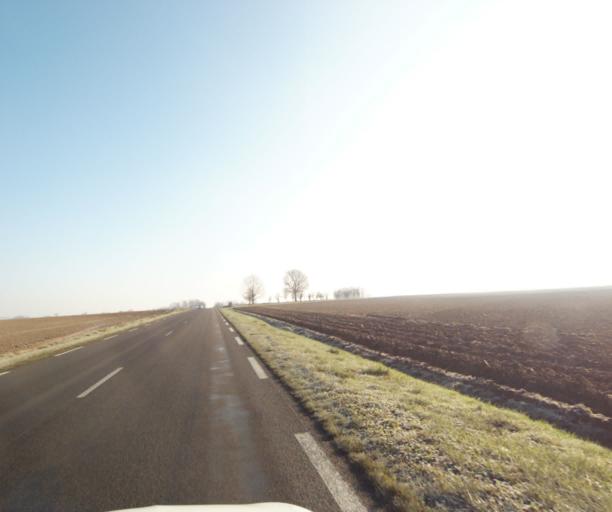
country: FR
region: Champagne-Ardenne
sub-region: Departement de la Haute-Marne
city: Montier-en-Der
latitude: 48.4316
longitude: 4.7020
